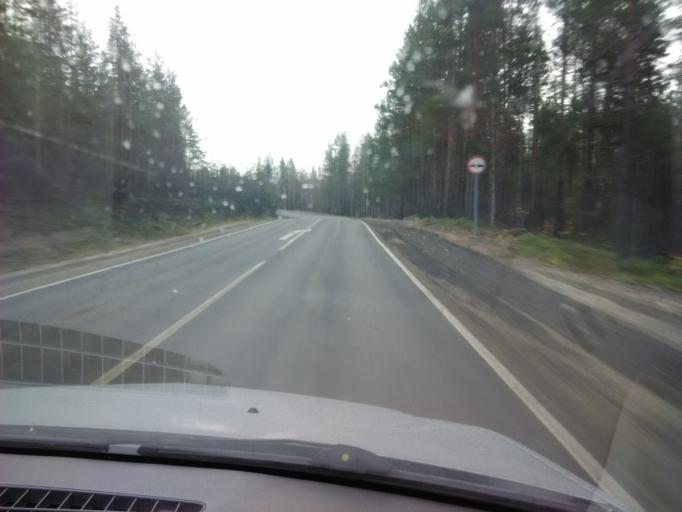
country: RU
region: Murmansk
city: Kandalaksha
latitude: 67.2518
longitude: 32.4320
